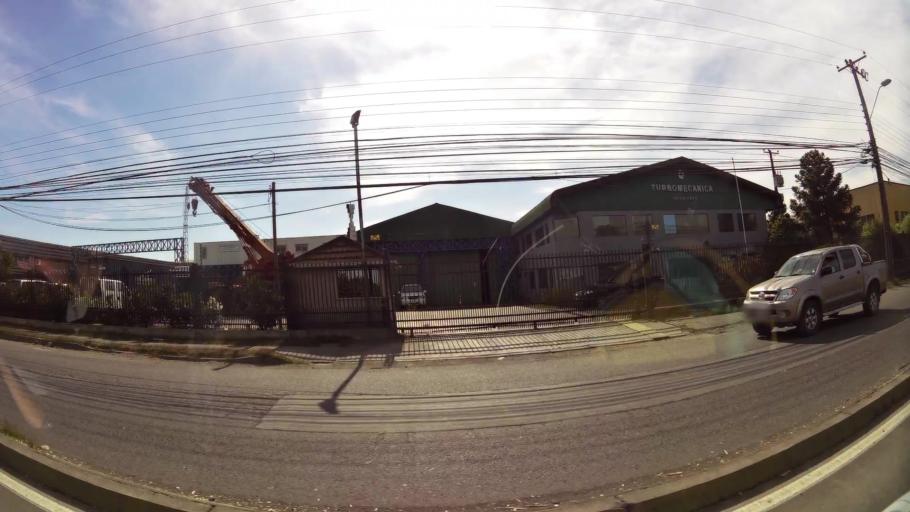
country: CL
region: Biobio
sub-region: Provincia de Concepcion
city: Talcahuano
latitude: -36.7646
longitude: -73.1170
